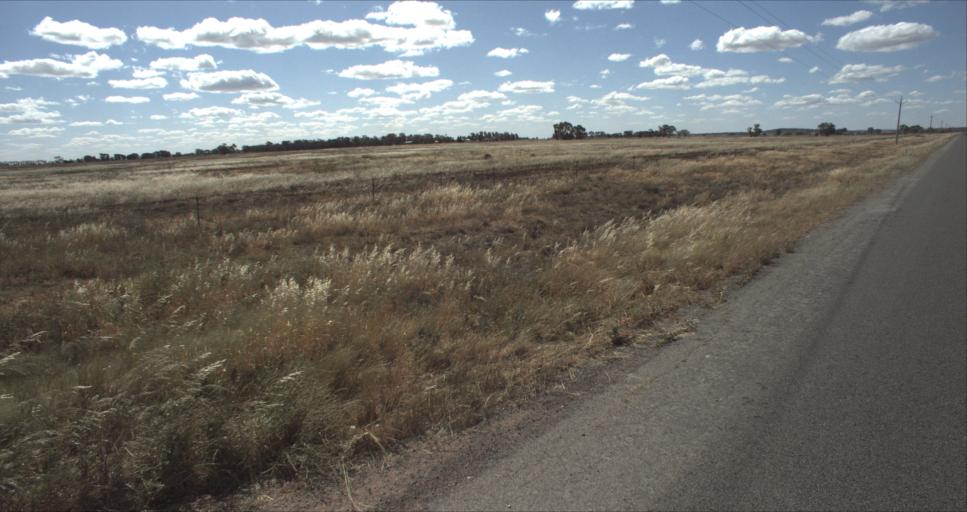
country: AU
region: New South Wales
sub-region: Leeton
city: Leeton
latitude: -34.4710
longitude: 146.2509
